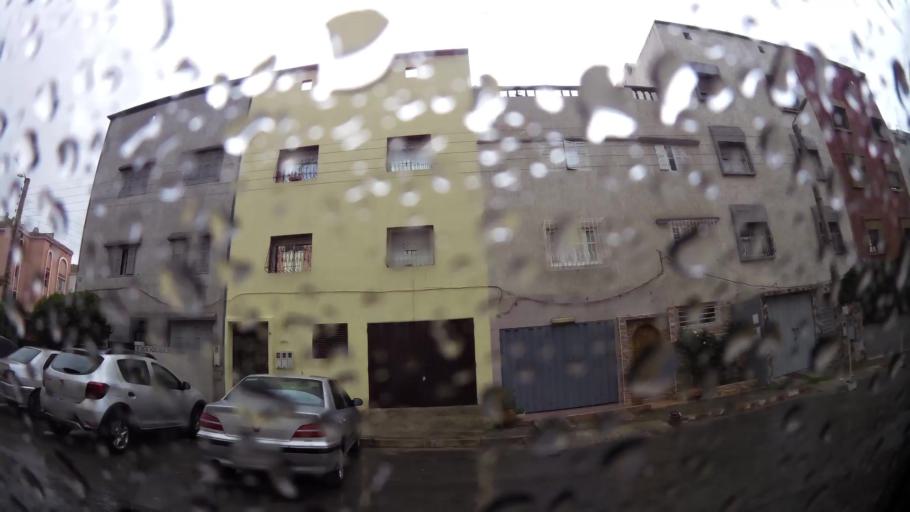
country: MA
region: Grand Casablanca
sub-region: Mediouna
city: Tit Mellil
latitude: 33.6144
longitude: -7.4976
